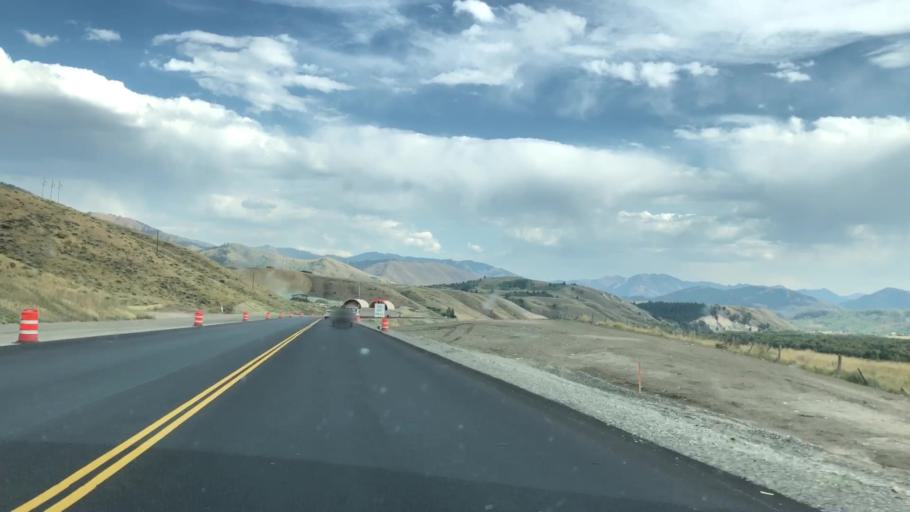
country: US
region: Wyoming
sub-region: Teton County
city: South Park
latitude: 43.4068
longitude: -110.7626
